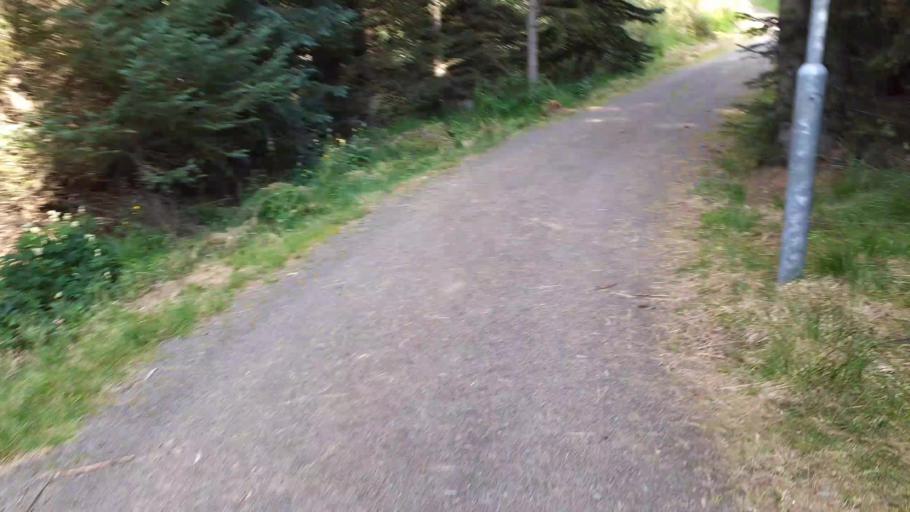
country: IS
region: Northeast
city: Akureyri
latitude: 65.6433
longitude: -18.0878
